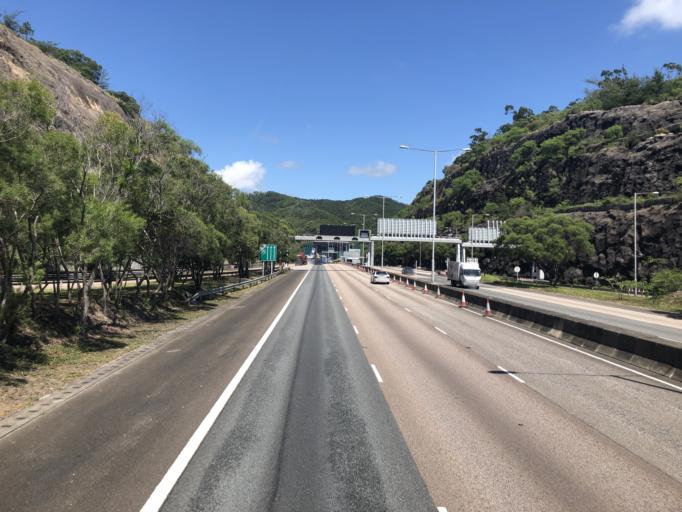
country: HK
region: Tsuen Wan
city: Tsuen Wan
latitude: 22.3721
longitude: 114.0724
